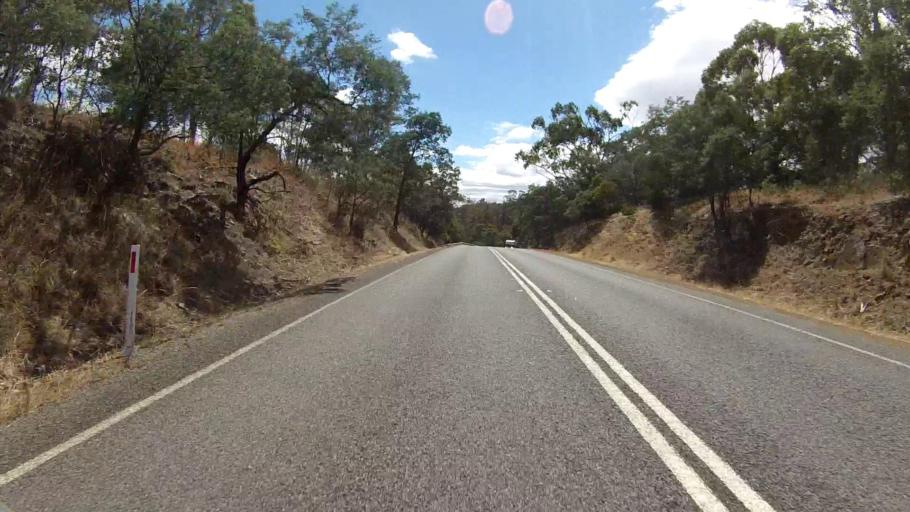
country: AU
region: Tasmania
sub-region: Sorell
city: Sorell
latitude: -42.6087
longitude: 147.6704
